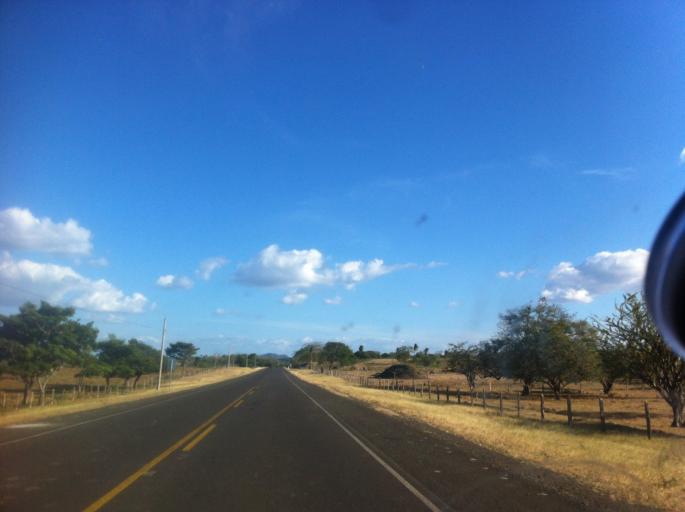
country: NI
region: Chontales
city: Acoyapa
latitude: 11.9202
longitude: -85.1316
